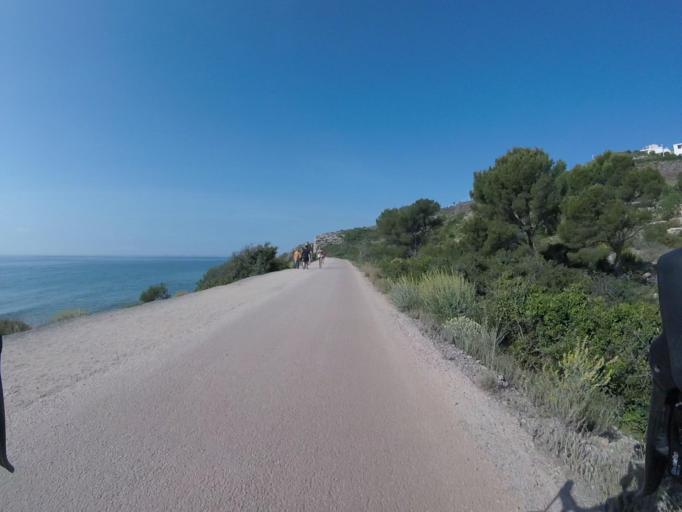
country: ES
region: Valencia
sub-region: Provincia de Castello
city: Benicassim
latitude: 40.0605
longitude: 0.1115
